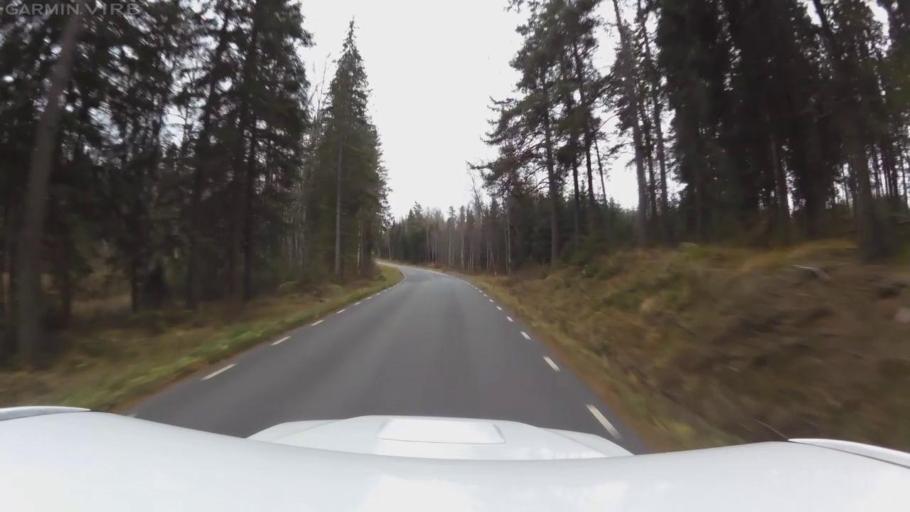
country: SE
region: OEstergoetland
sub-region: Mjolby Kommun
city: Mantorp
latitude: 58.1669
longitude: 15.3969
